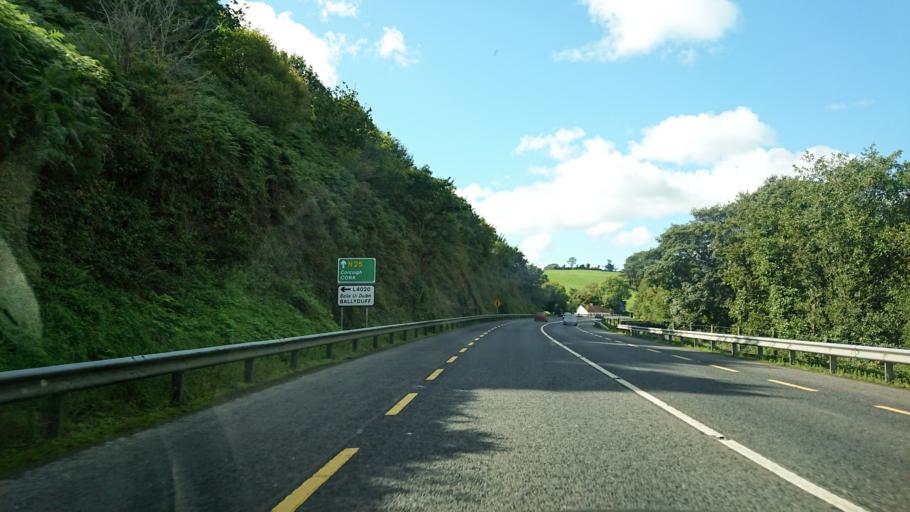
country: IE
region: Munster
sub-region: Waterford
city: Portlaw
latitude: 52.2378
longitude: -7.2845
